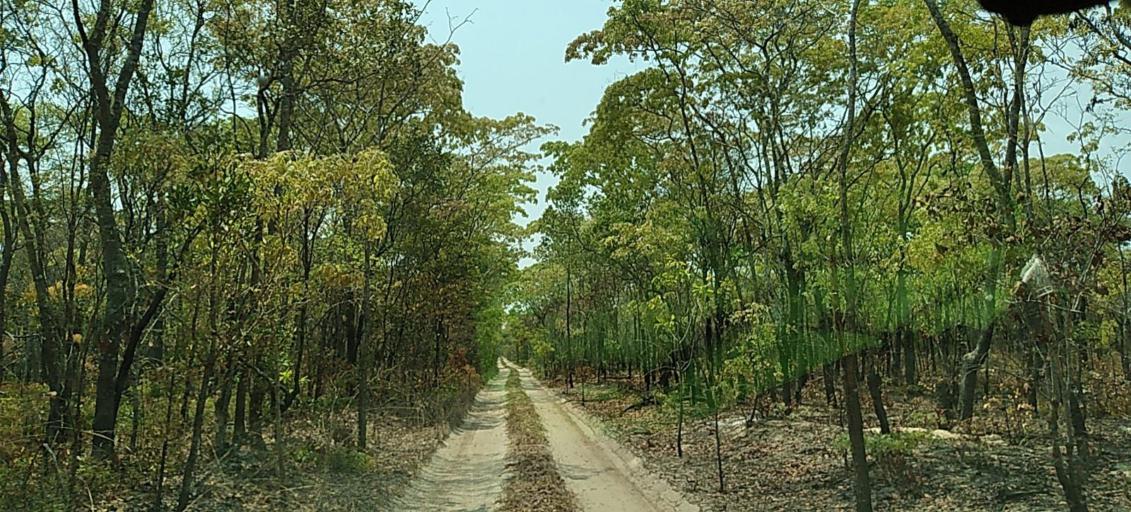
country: ZM
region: North-Western
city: Kabompo
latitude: -13.6511
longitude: 24.4730
